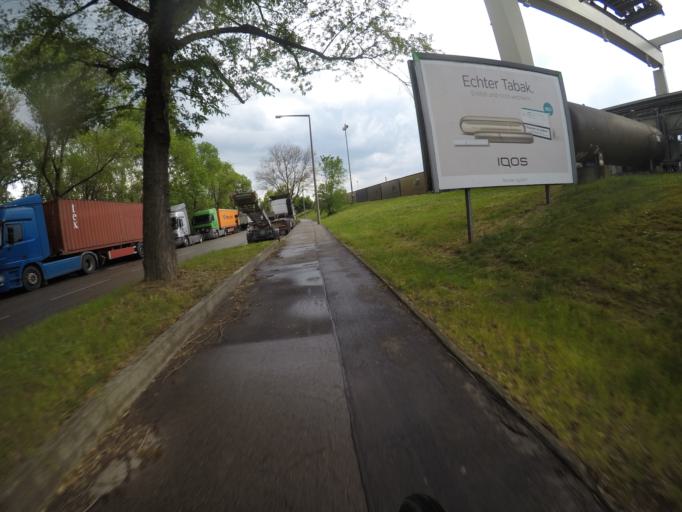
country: DE
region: Baden-Wuerttemberg
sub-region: Regierungsbezirk Stuttgart
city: Fellbach
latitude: 48.7695
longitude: 9.2608
